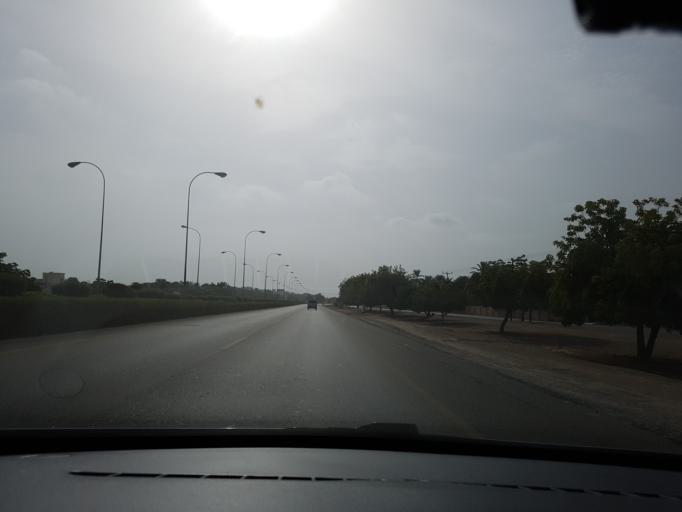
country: OM
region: Al Batinah
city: Al Sohar
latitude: 24.3935
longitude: 56.6873
